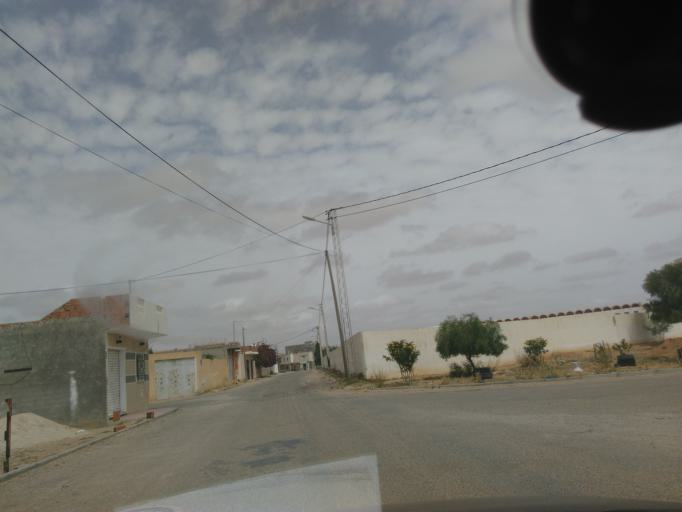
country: TN
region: Tataouine
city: Tataouine
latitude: 32.9483
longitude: 10.4719
